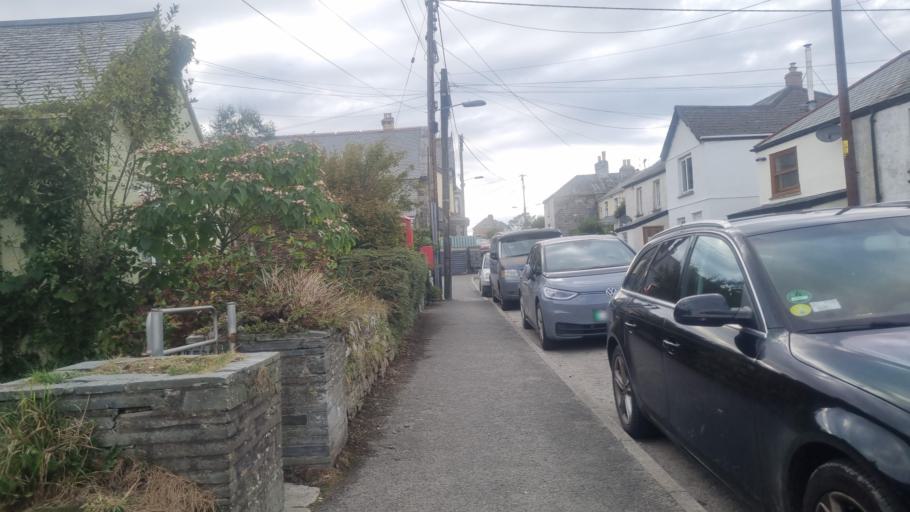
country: GB
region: England
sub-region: Cornwall
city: Camelford
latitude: 50.6209
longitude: -4.7267
